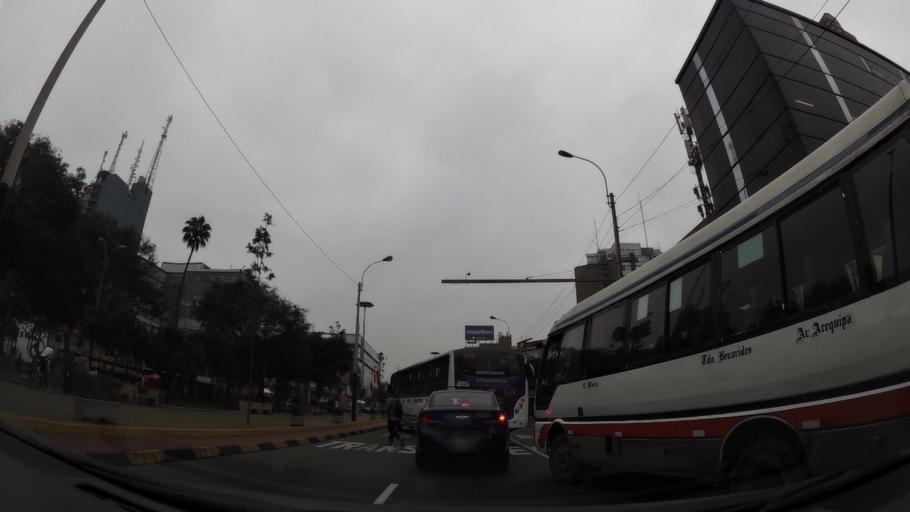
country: PE
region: Lima
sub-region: Lima
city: San Isidro
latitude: -12.1204
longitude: -77.0290
